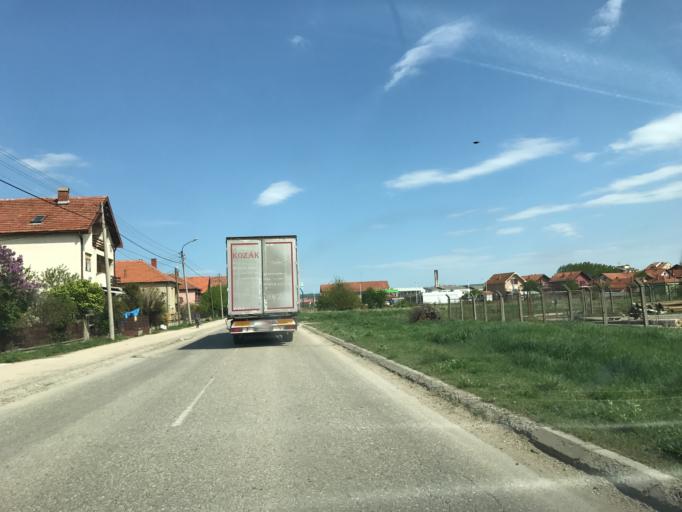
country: RS
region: Central Serbia
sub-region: Zajecarski Okrug
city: Zajecar
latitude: 43.9106
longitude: 22.2573
